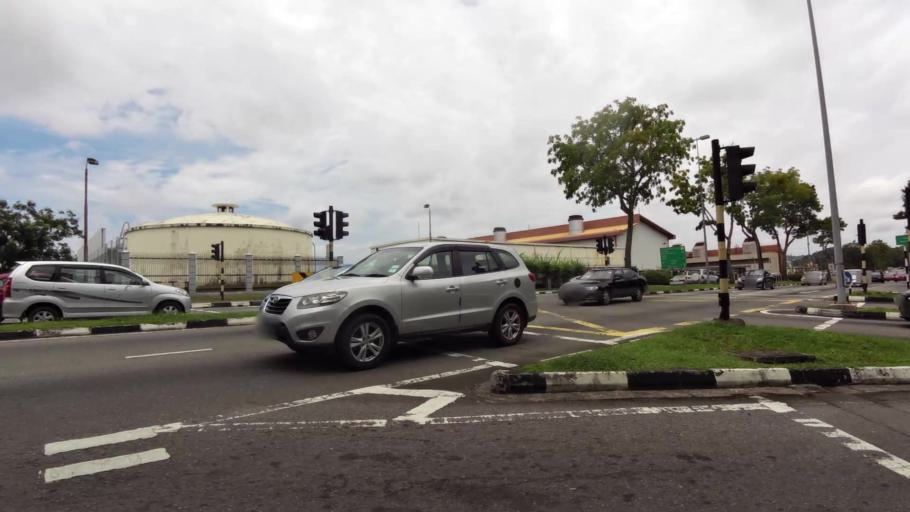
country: BN
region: Brunei and Muara
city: Bandar Seri Begawan
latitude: 4.9092
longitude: 114.9128
